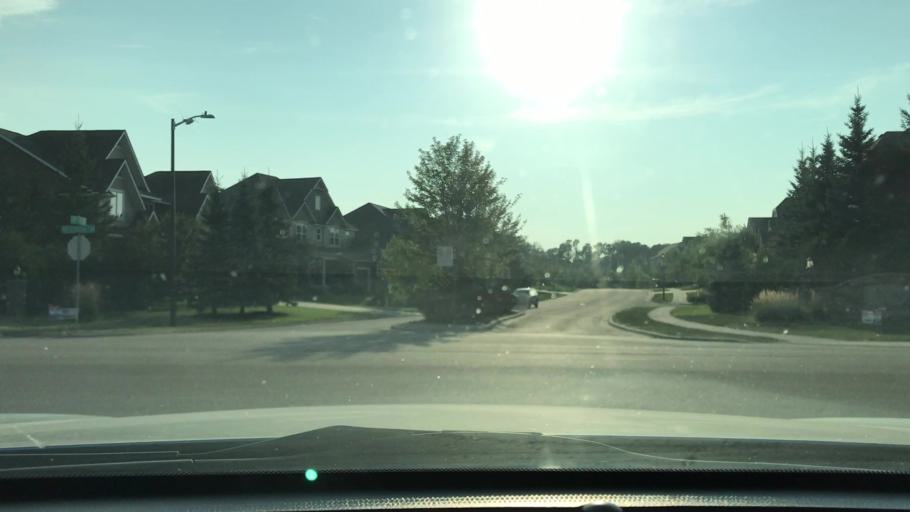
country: US
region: Minnesota
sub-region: Hennepin County
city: Maple Grove
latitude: 45.0541
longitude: -93.4816
